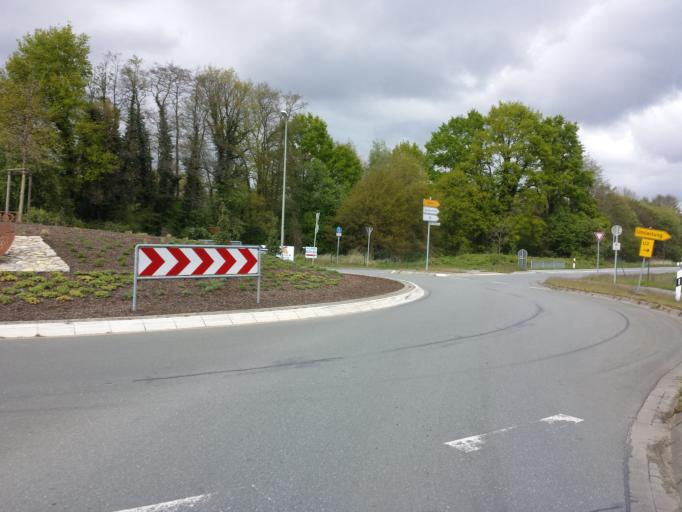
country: DE
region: North Rhine-Westphalia
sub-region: Regierungsbezirk Detmold
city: Harsewinkel
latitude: 51.9430
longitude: 8.2894
